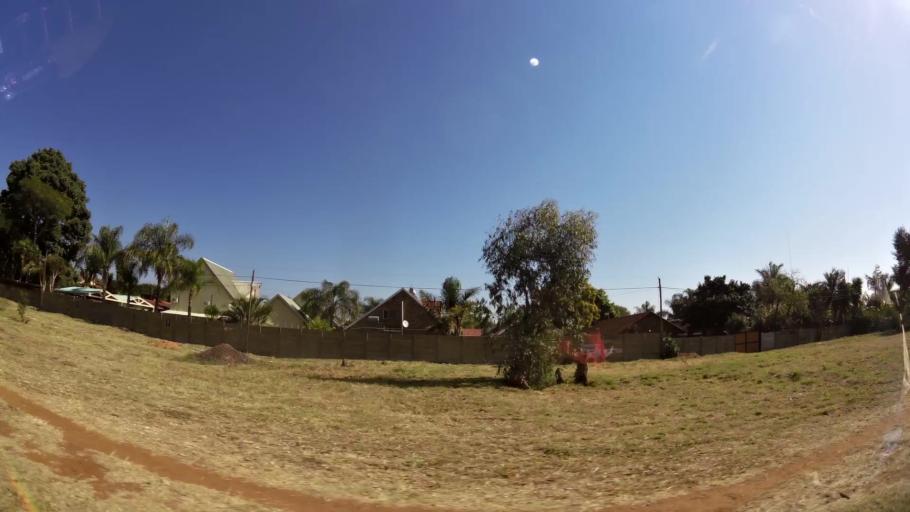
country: ZA
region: Gauteng
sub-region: City of Tshwane Metropolitan Municipality
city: Pretoria
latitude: -25.6827
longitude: 28.2424
